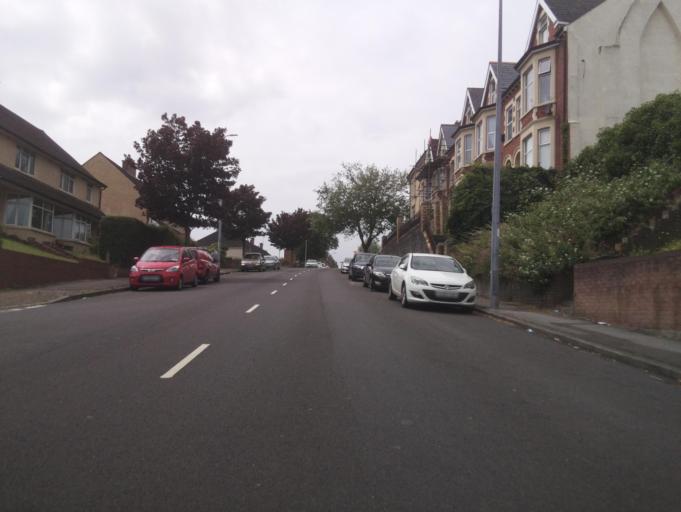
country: GB
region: Wales
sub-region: Vale of Glamorgan
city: Barry
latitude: 51.4090
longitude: -3.2563
